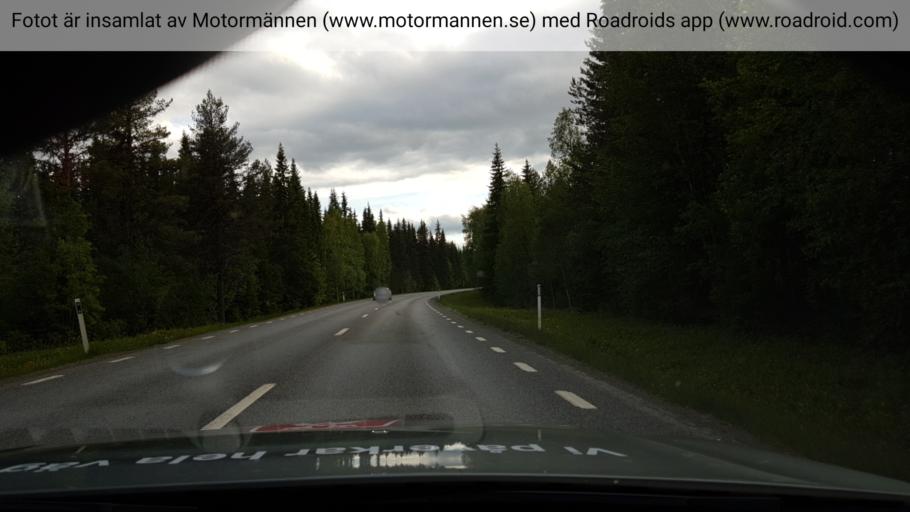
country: SE
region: Jaemtland
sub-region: Stroemsunds Kommun
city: Stroemsund
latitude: 63.5247
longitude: 15.3191
